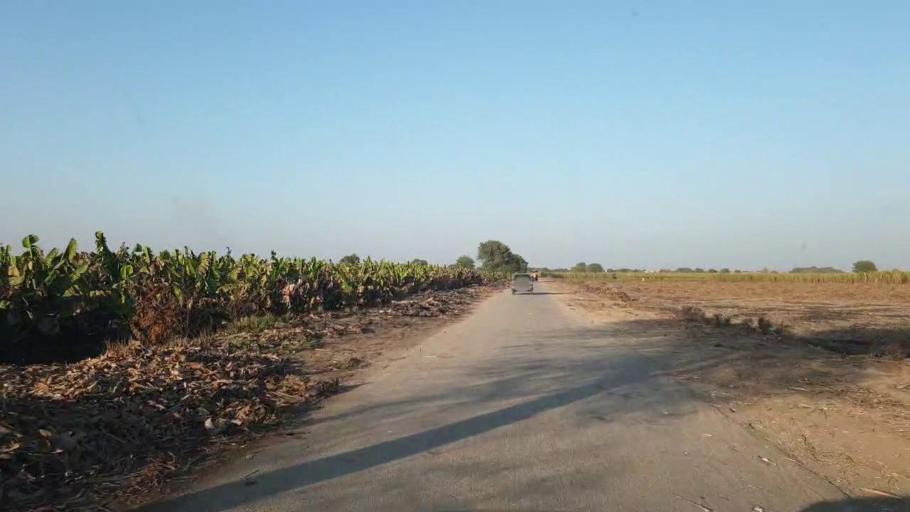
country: PK
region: Sindh
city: Chambar
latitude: 25.3577
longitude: 68.7380
